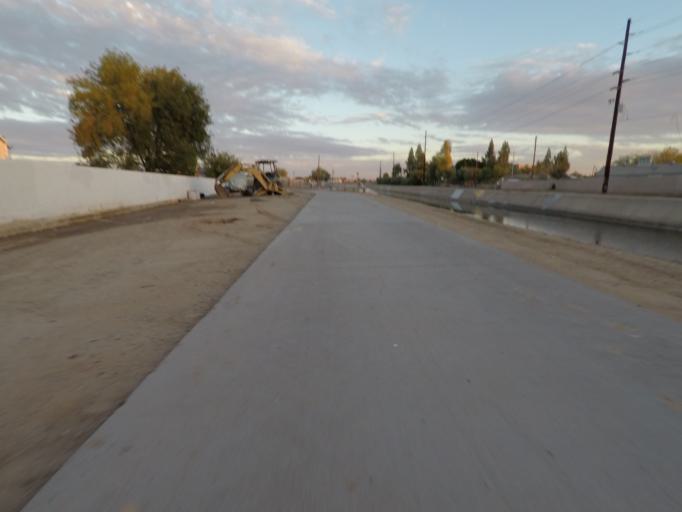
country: US
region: Arizona
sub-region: Maricopa County
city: Phoenix
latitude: 33.4978
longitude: -112.0527
